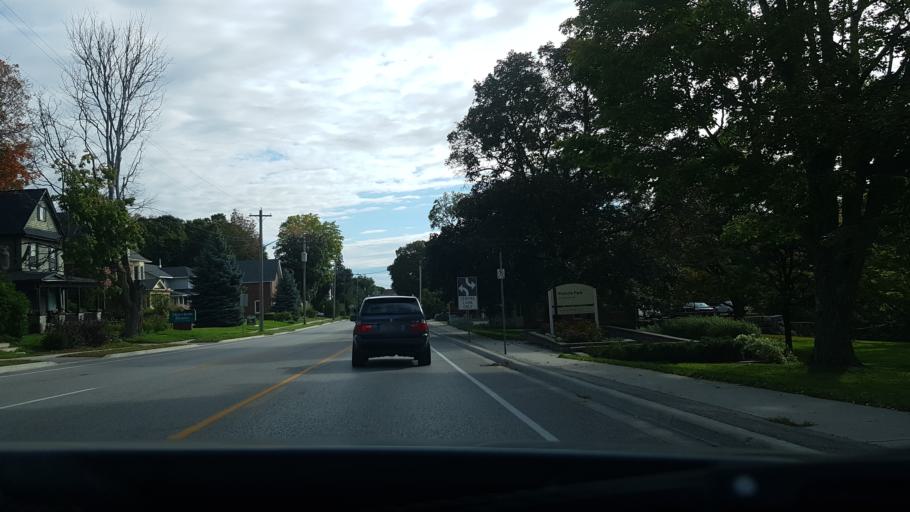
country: CA
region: Ontario
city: Orillia
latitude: 44.6093
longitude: -79.4256
